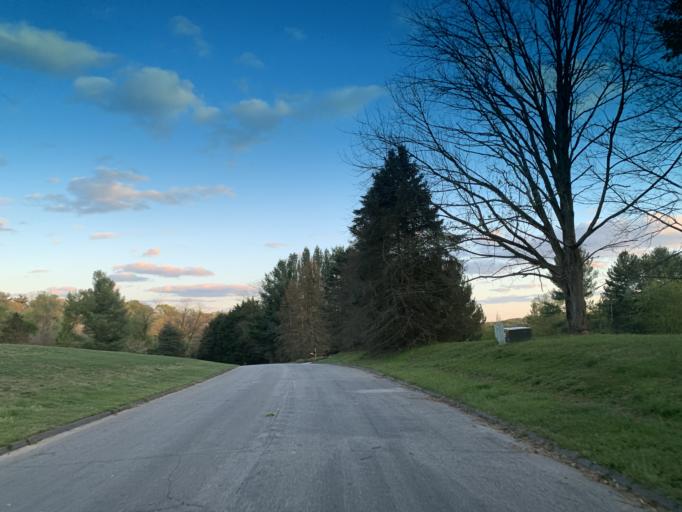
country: US
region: Pennsylvania
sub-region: York County
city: Susquehanna Trails
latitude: 39.6875
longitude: -76.3512
